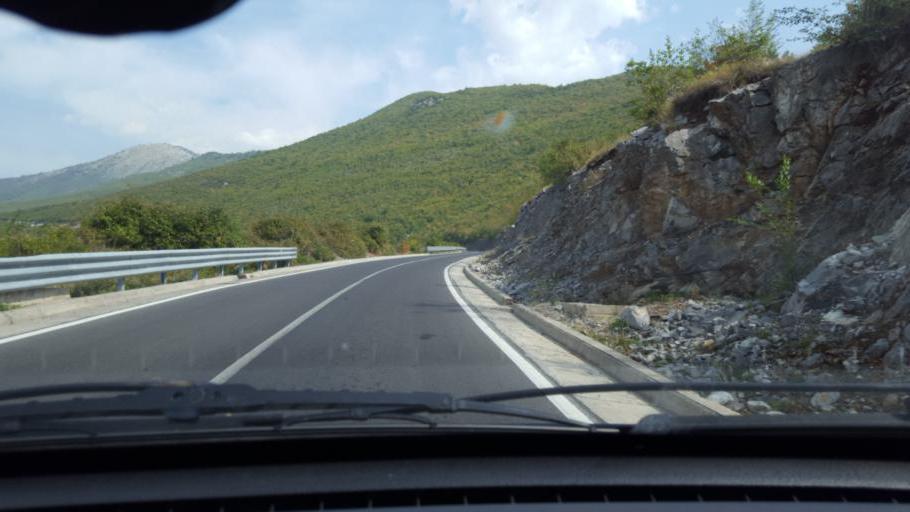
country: AL
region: Shkoder
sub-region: Rrethi i Malesia e Madhe
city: Kastrat
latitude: 42.3723
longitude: 19.4778
